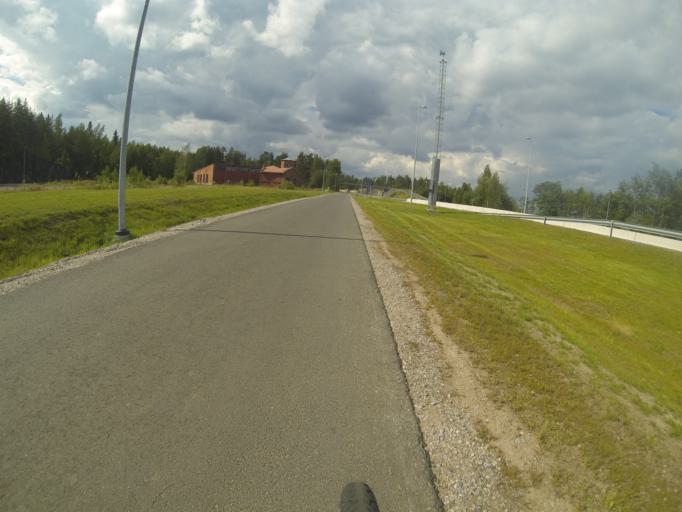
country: FI
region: Southern Savonia
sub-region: Savonlinna
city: Savonlinna
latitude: 61.8768
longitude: 28.8739
